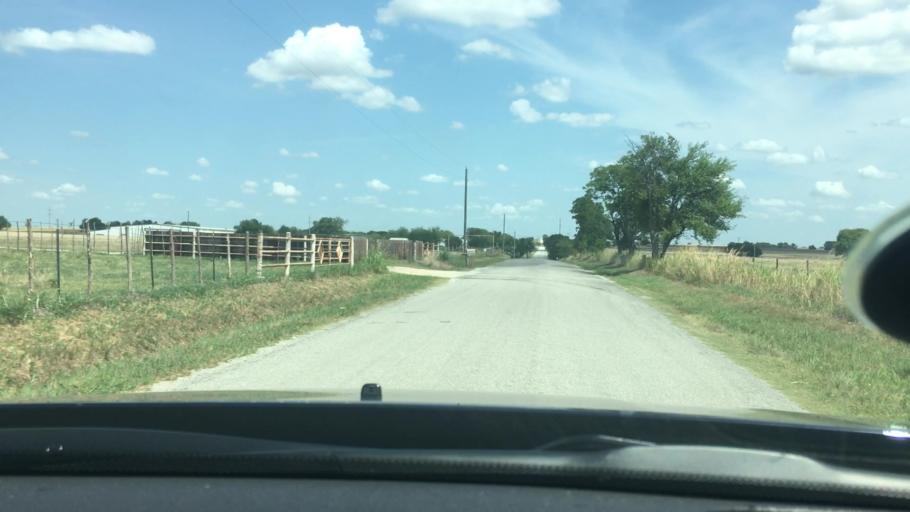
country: US
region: Oklahoma
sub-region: Love County
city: Marietta
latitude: 33.9433
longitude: -97.1869
